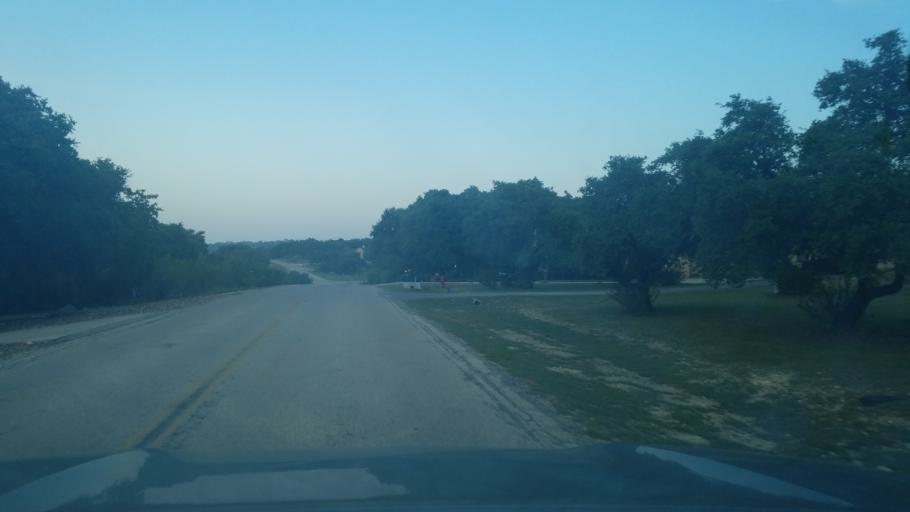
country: US
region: Texas
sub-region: Comal County
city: Bulverde
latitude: 29.8262
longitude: -98.4028
